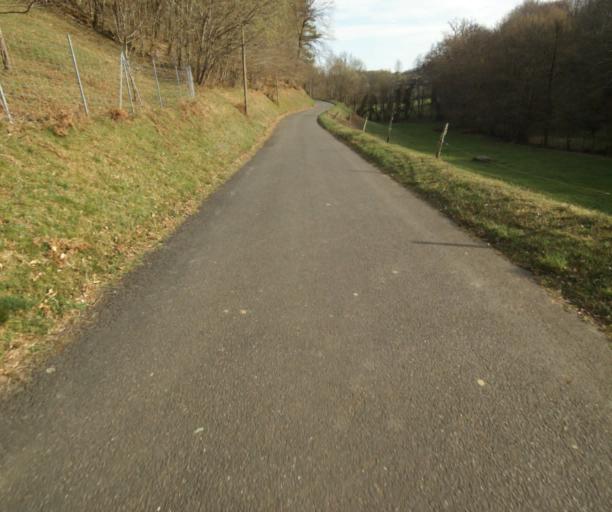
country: FR
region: Limousin
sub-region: Departement de la Correze
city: Naves
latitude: 45.2963
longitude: 1.7560
